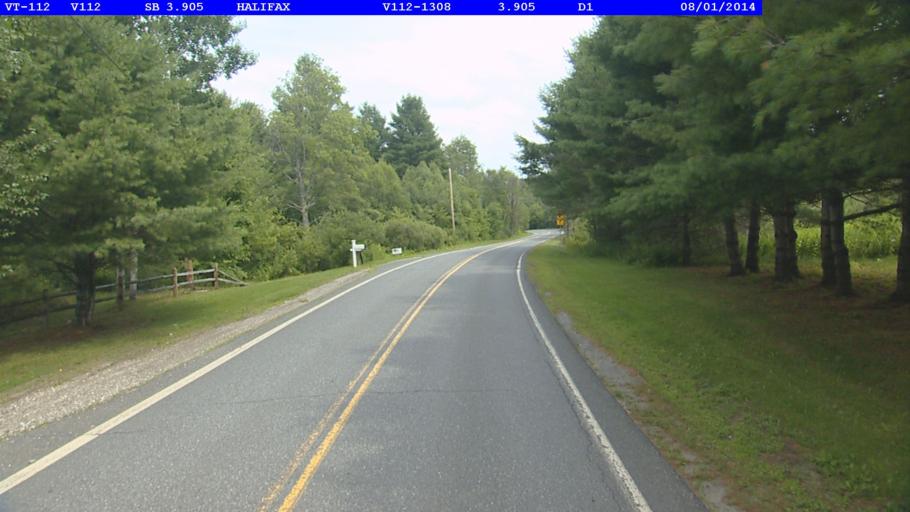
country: US
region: Massachusetts
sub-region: Franklin County
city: Colrain
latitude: 42.7613
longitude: -72.7800
